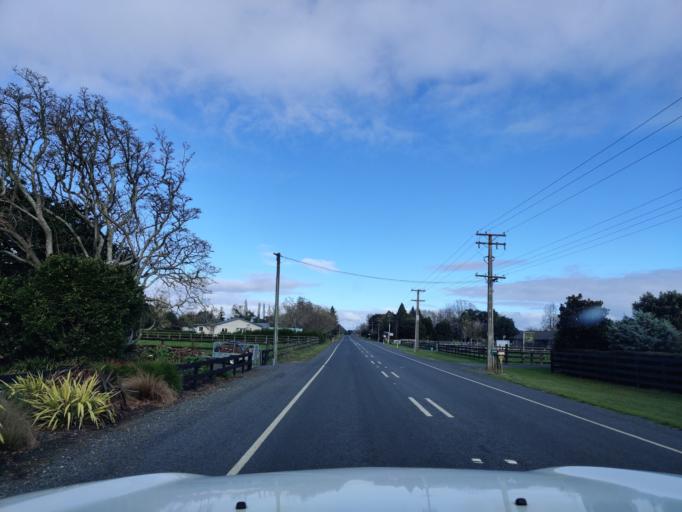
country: NZ
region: Waikato
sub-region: Waipa District
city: Cambridge
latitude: -37.8796
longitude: 175.4389
